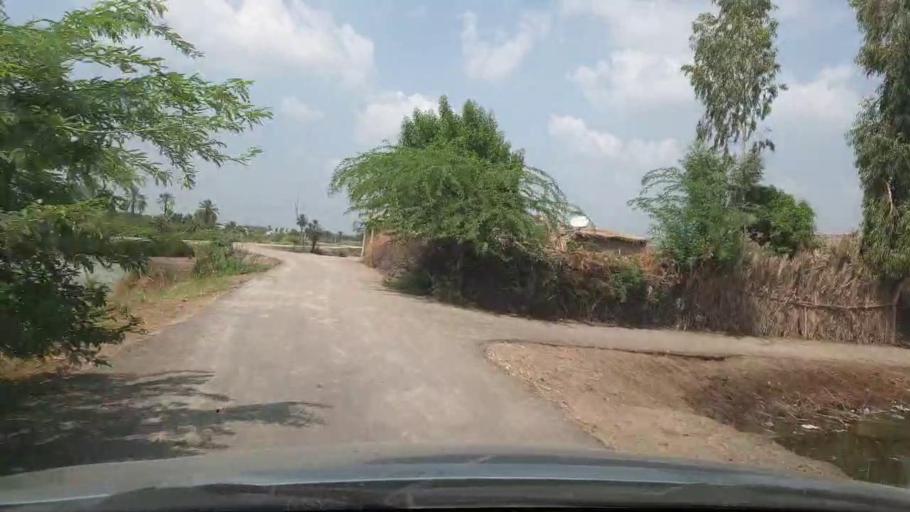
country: PK
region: Sindh
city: Kot Diji
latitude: 27.3999
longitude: 68.7381
